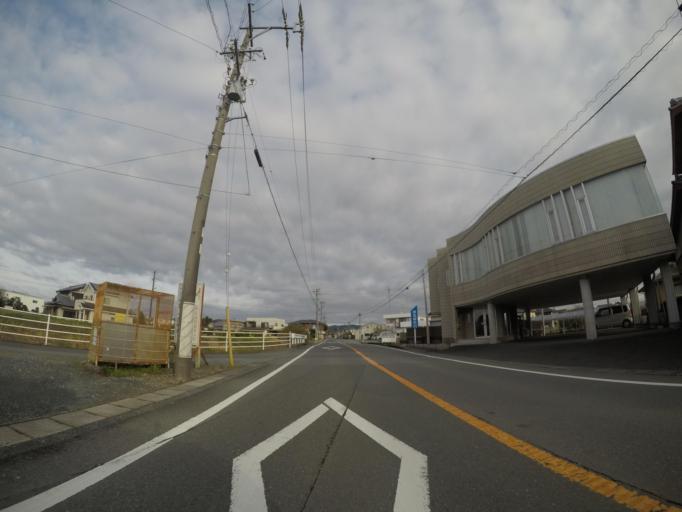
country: JP
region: Shizuoka
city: Hamakita
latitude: 34.8156
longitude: 137.7775
